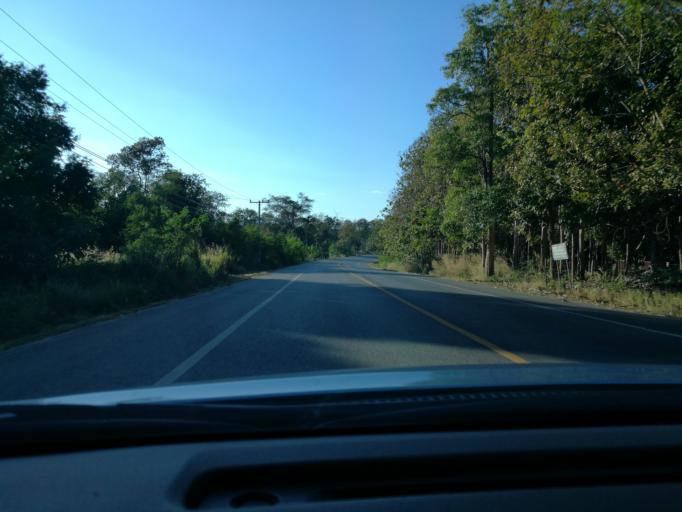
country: TH
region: Phitsanulok
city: Nakhon Thai
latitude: 17.0696
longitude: 100.8403
